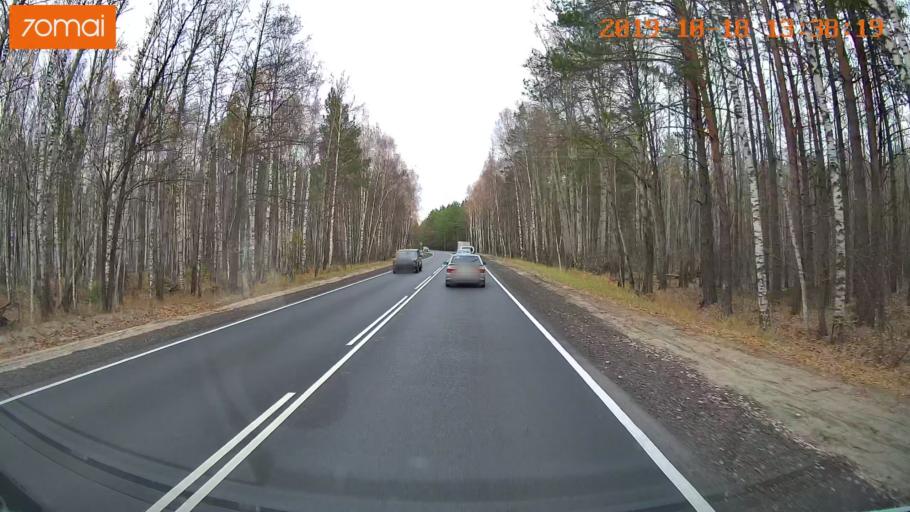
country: RU
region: Rjazan
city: Solotcha
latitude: 54.8879
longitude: 40.0022
